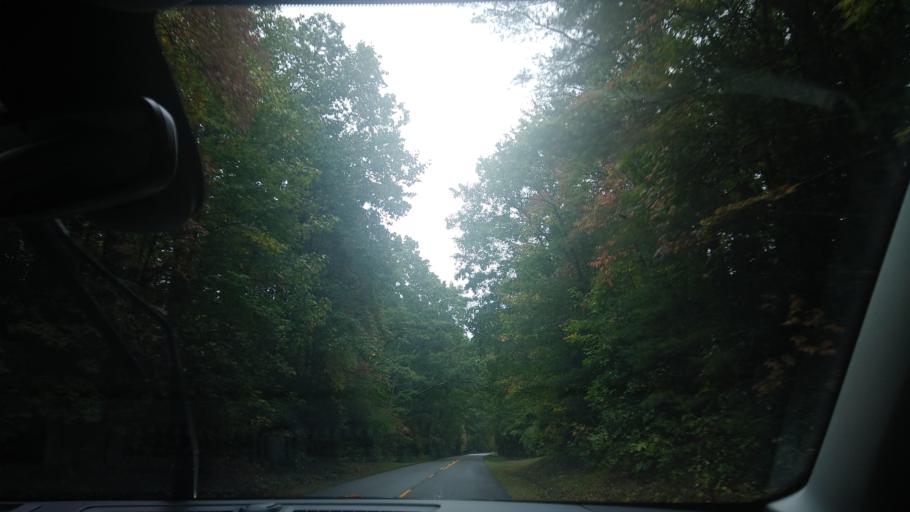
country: US
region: North Carolina
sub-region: Mitchell County
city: Spruce Pine
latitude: 35.8902
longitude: -81.9805
